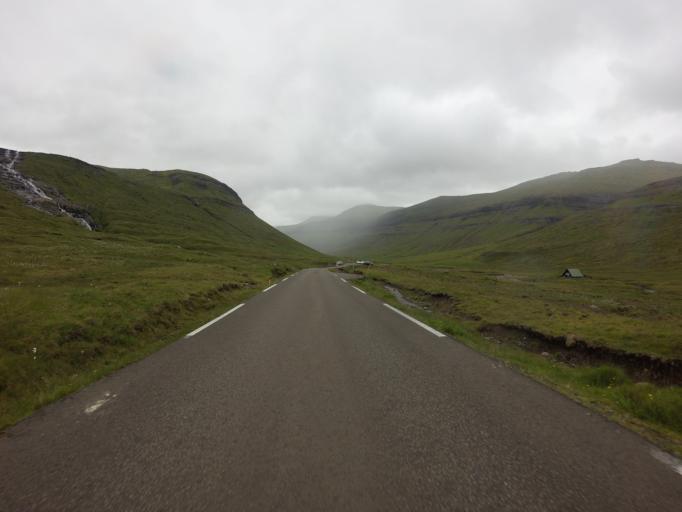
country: FO
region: Streymoy
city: Vestmanna
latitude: 62.2215
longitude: -7.1281
